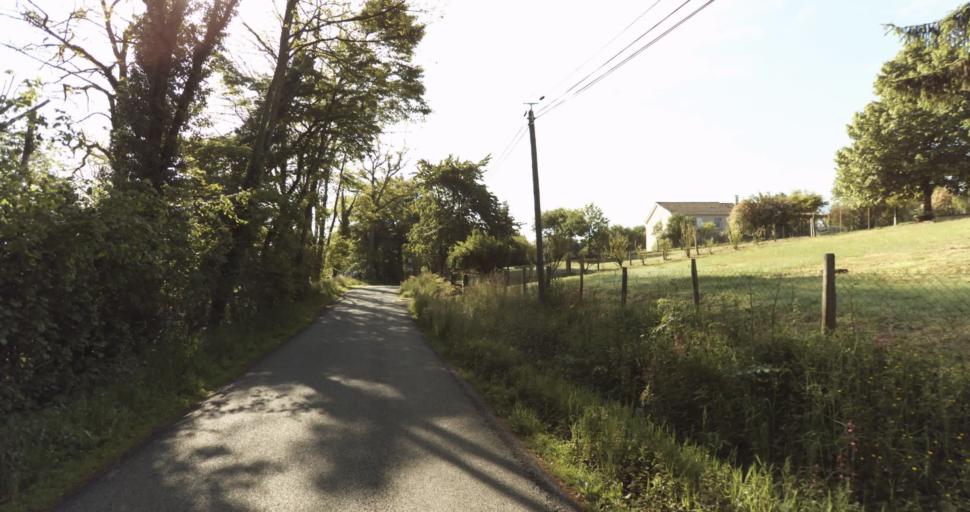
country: FR
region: Limousin
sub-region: Departement de la Haute-Vienne
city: Solignac
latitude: 45.7390
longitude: 1.2736
